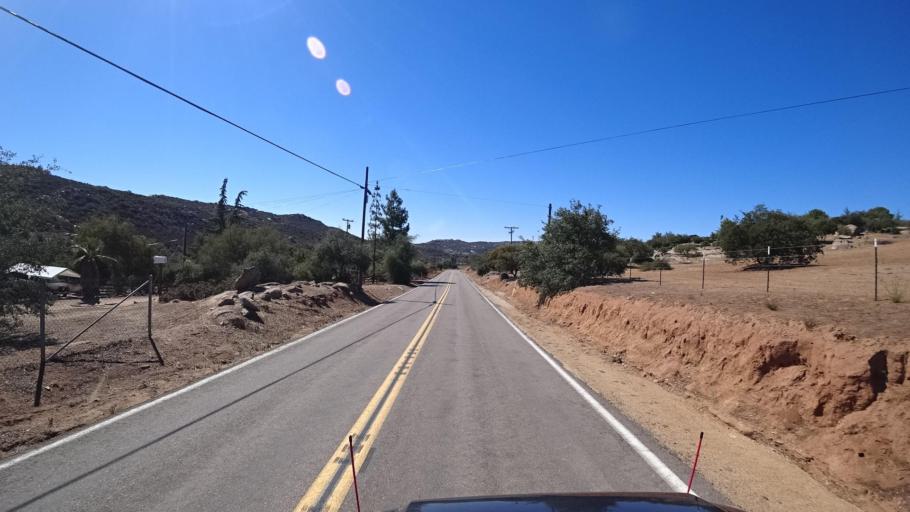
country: US
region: California
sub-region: San Diego County
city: Descanso
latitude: 32.7721
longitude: -116.6715
